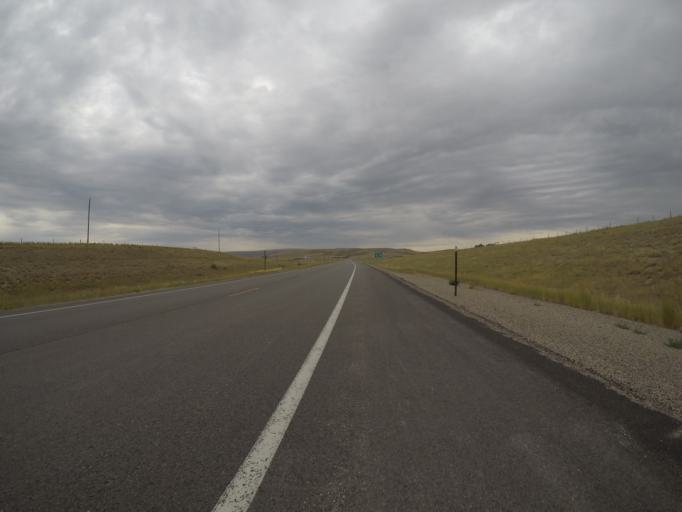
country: US
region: Wyoming
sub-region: Lincoln County
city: Kemmerer
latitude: 41.7955
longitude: -110.5888
